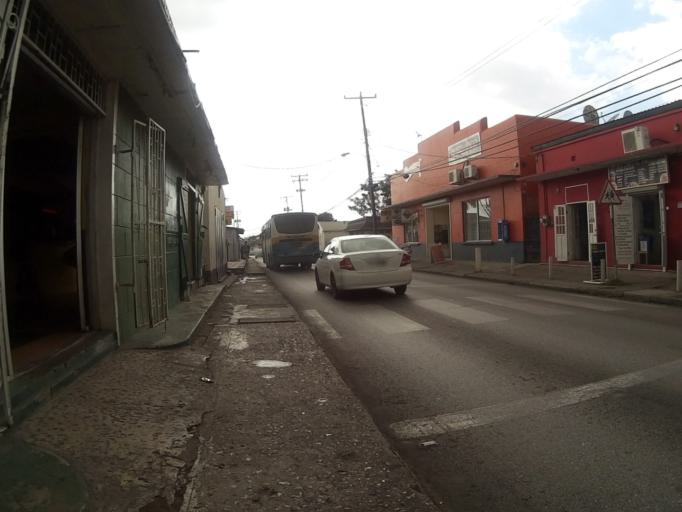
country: BB
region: Saint Michael
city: Bridgetown
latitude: 13.1026
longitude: -59.6040
